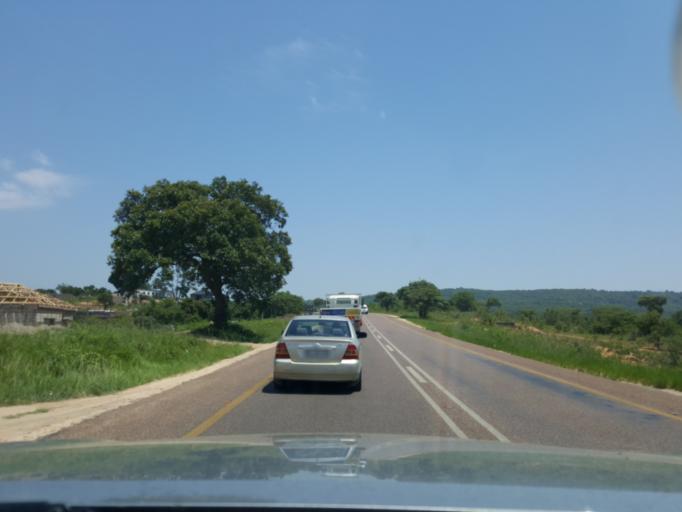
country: ZA
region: Limpopo
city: Thulamahashi
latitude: -24.8968
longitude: 31.1067
